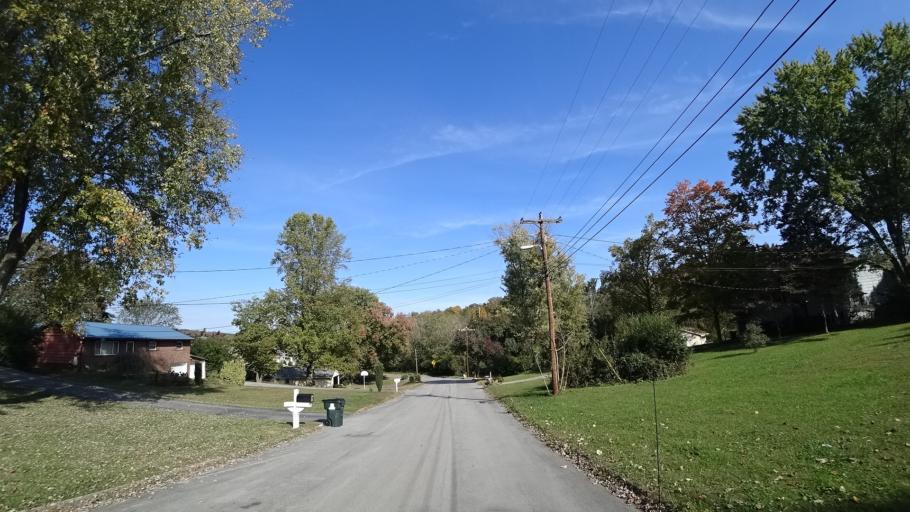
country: US
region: Tennessee
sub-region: Knox County
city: Farragut
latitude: 35.9285
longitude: -84.1500
